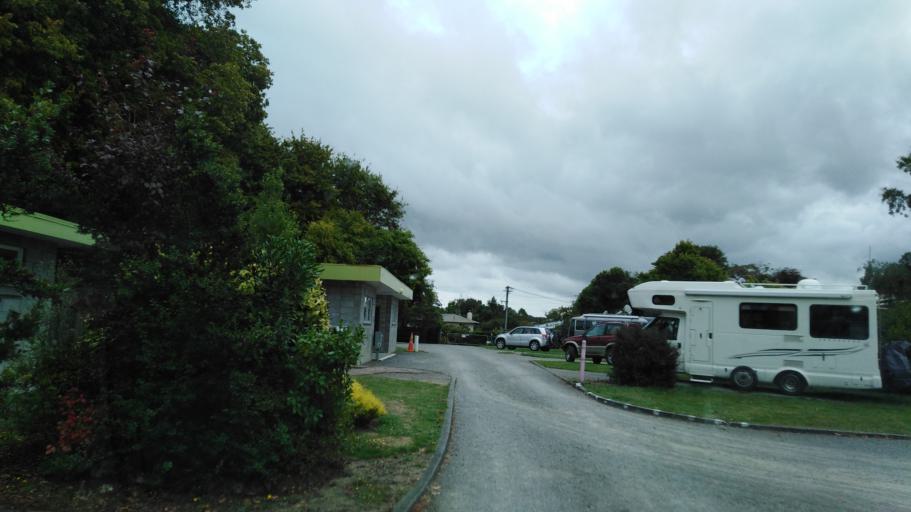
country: NZ
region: Manawatu-Wanganui
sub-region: Rangitikei District
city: Bulls
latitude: -40.0655
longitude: 175.3769
